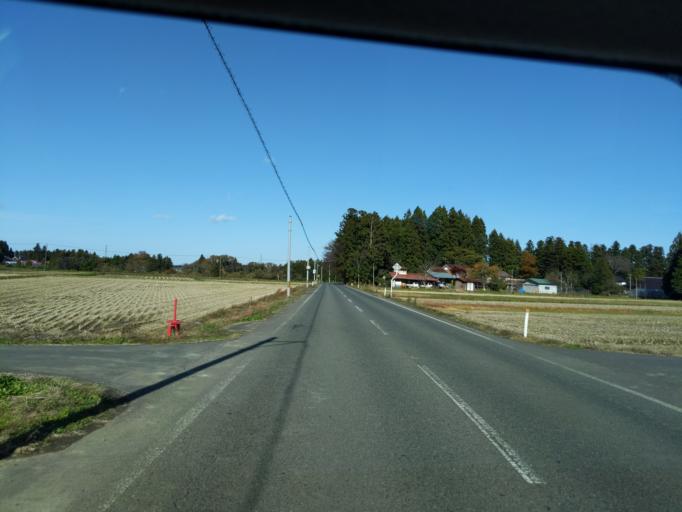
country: JP
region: Iwate
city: Mizusawa
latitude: 39.0882
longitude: 141.0937
